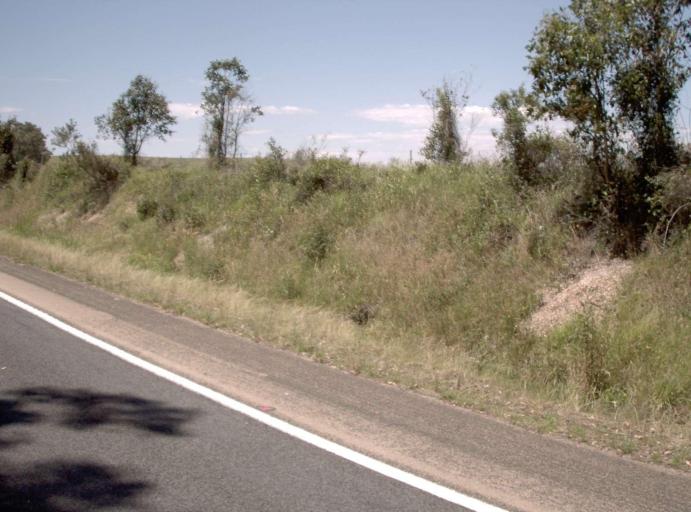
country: AU
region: Victoria
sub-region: East Gippsland
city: Lakes Entrance
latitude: -37.7040
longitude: 148.5150
